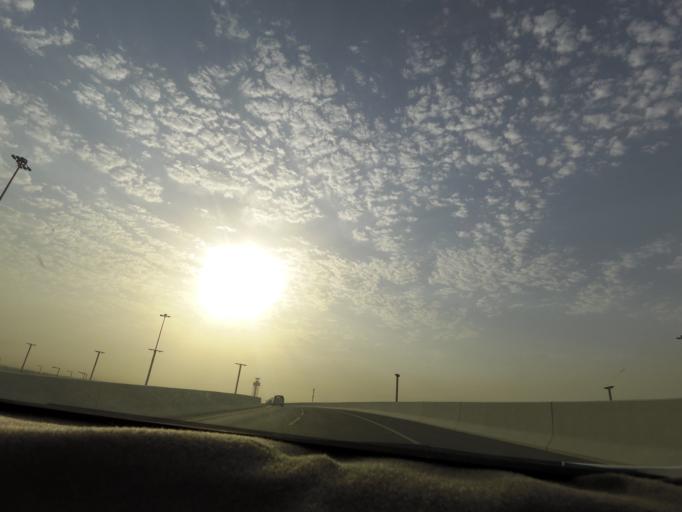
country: QA
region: Al Wakrah
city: Al Wakrah
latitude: 25.2378
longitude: 51.5915
